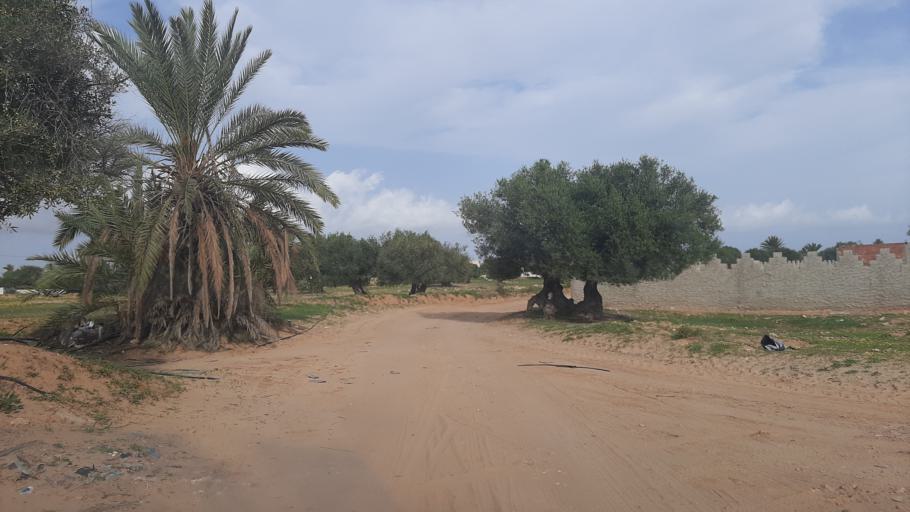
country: TN
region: Madanin
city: Midoun
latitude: 33.8074
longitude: 11.0237
